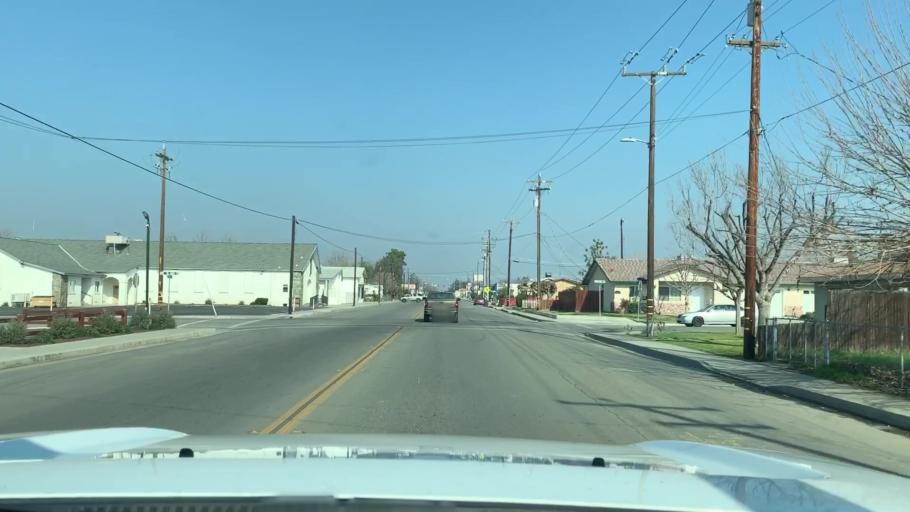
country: US
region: California
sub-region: Kern County
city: Shafter
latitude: 35.4959
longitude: -119.2783
